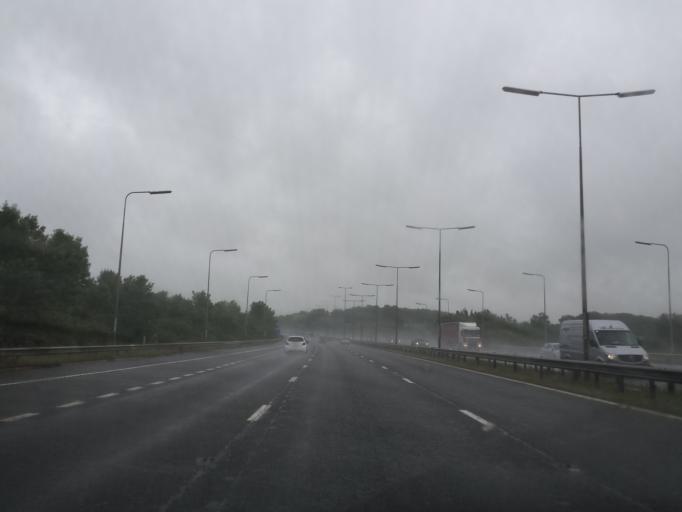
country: GB
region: England
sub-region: Leicestershire
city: Kegworth
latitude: 52.8119
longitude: -1.3061
